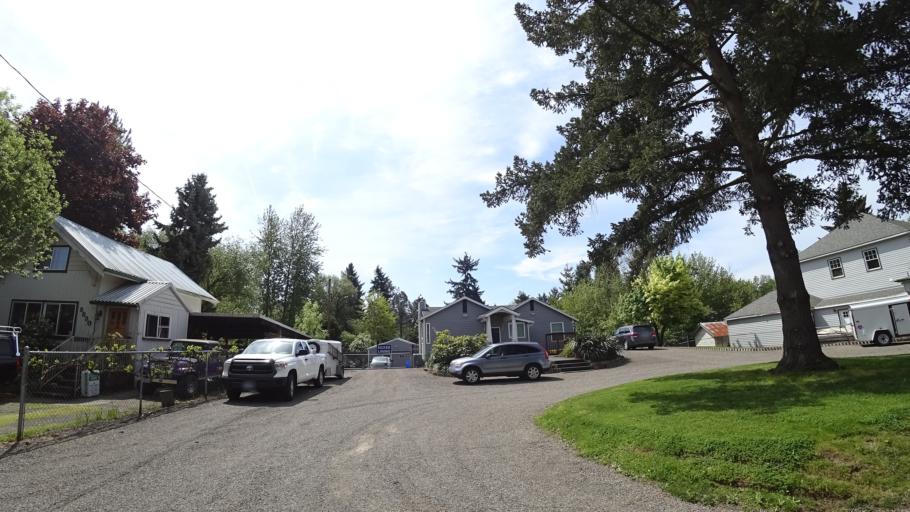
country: US
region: Oregon
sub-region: Clackamas County
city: Milwaukie
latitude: 45.4567
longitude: -122.6036
